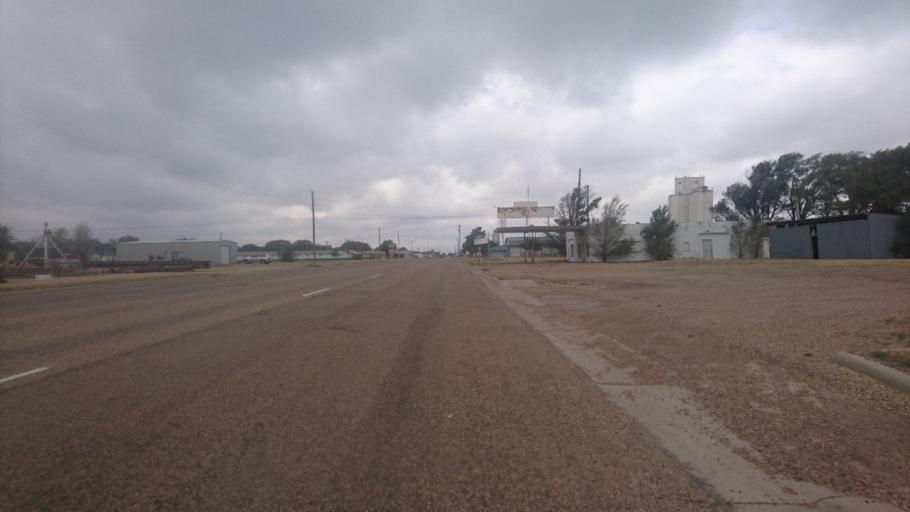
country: US
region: Texas
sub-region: Oldham County
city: Vega
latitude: 35.2431
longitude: -102.4219
